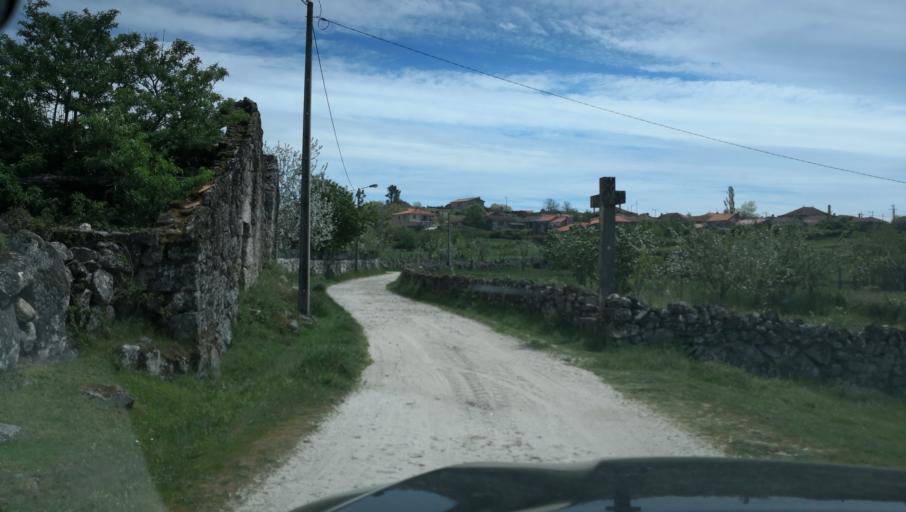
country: PT
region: Vila Real
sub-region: Vila Real
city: Vila Real
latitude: 41.3731
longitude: -7.6561
